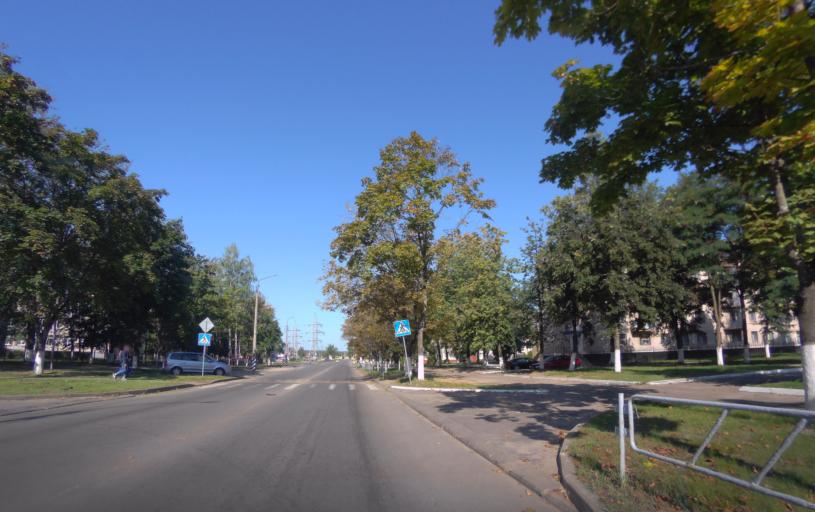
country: BY
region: Minsk
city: Horad Barysaw
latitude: 54.2153
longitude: 28.4812
